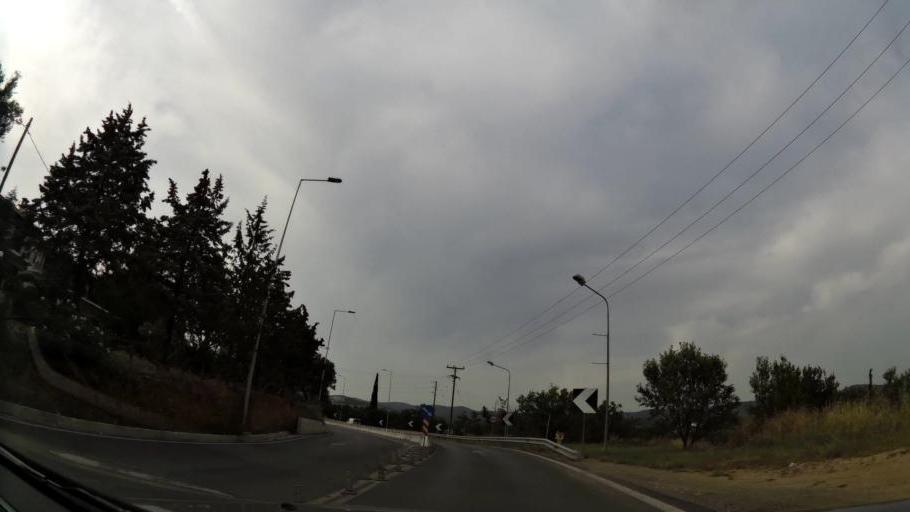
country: GR
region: Central Macedonia
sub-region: Nomos Thessalonikis
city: Oraiokastro
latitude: 40.7164
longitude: 22.9294
